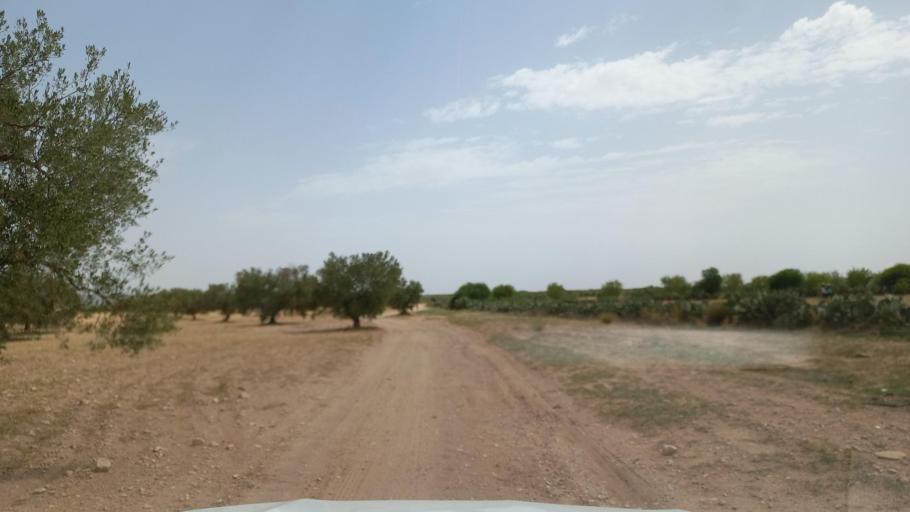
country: TN
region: Al Qasrayn
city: Kasserine
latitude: 35.2907
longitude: 9.0213
